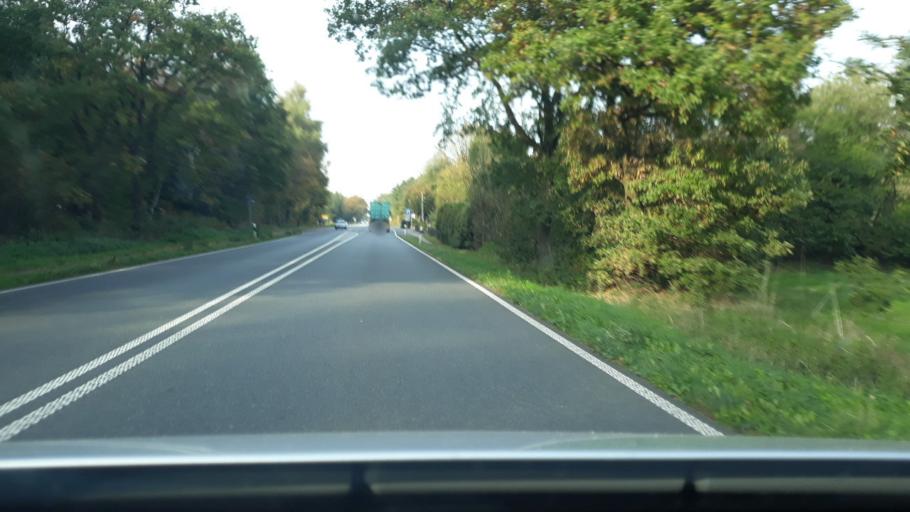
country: DE
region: Schleswig-Holstein
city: Kropp
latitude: 54.4041
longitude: 9.5346
